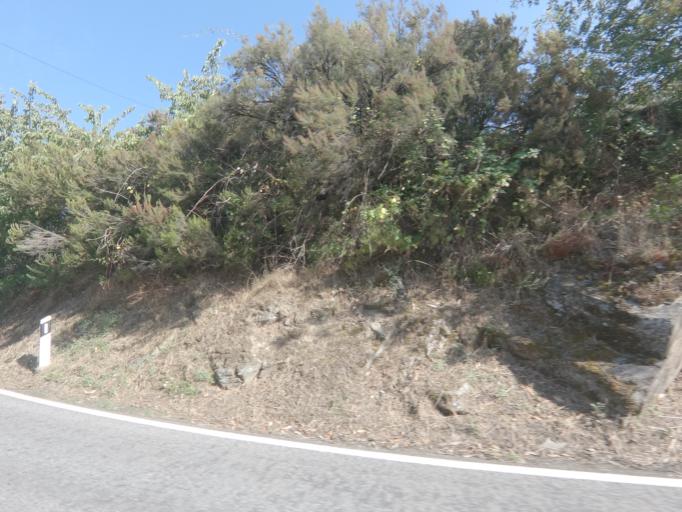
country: PT
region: Viseu
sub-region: Tabuaco
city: Tabuaco
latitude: 41.1202
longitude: -7.5680
